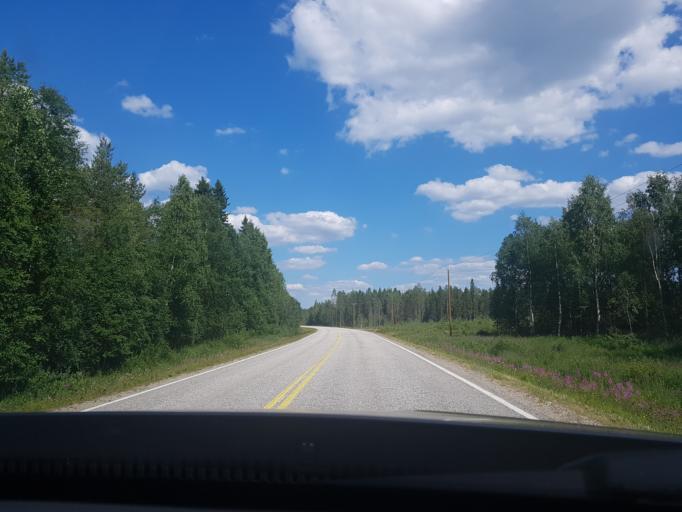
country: FI
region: Kainuu
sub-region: Kehys-Kainuu
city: Kuhmo
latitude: 64.2194
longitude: 29.7936
